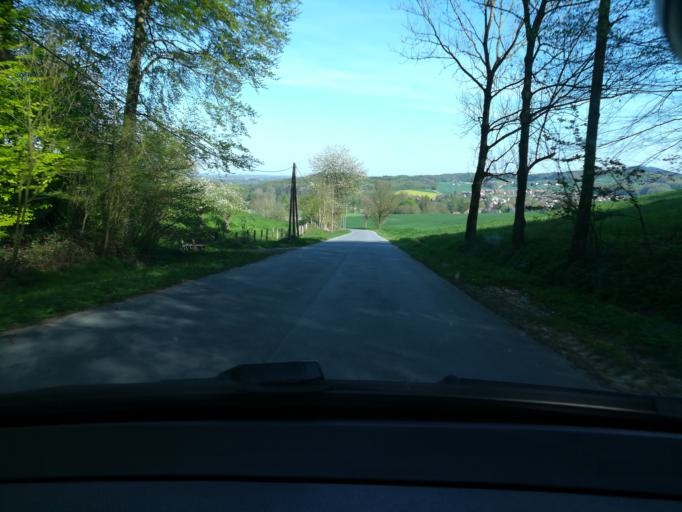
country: DE
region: North Rhine-Westphalia
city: Borgholzhausen
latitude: 52.1090
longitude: 8.2916
